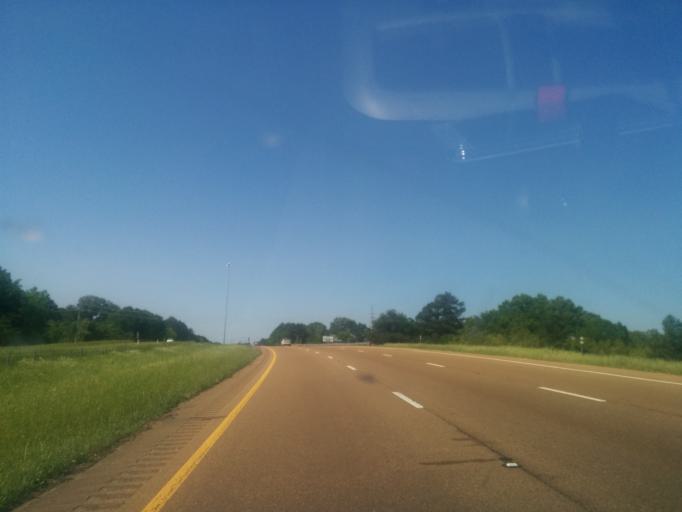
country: US
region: Mississippi
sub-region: Hinds County
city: Jackson
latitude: 32.3047
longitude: -90.2452
